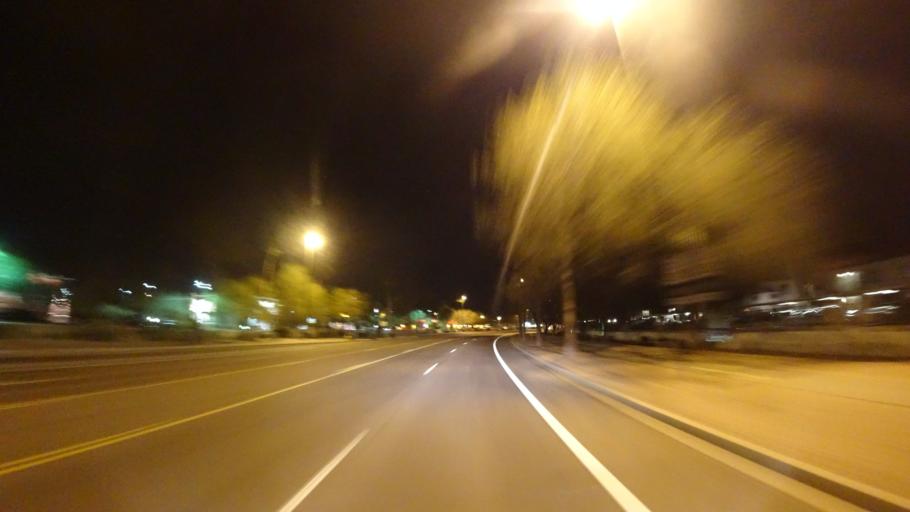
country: US
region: Arizona
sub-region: Maricopa County
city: Gilbert
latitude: 33.3848
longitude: -111.6896
